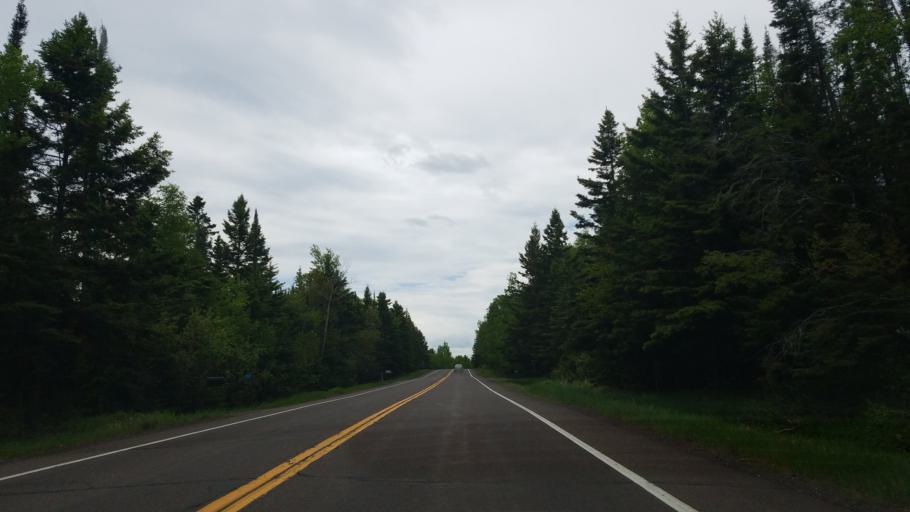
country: US
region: Minnesota
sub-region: Lake County
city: Two Harbors
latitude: 47.0548
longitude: -91.6201
